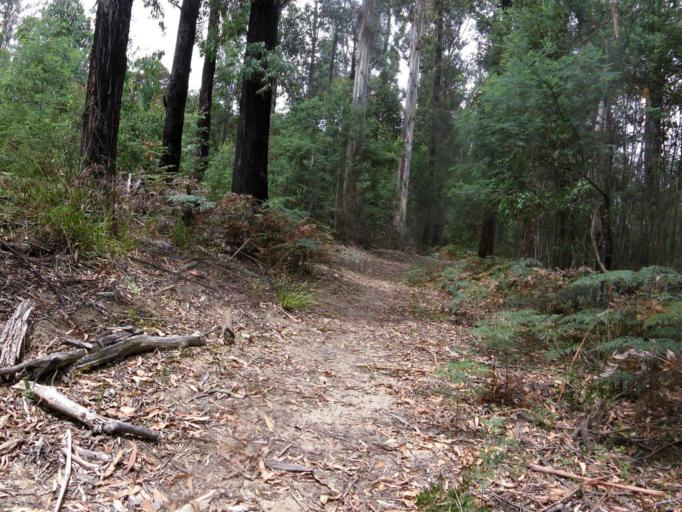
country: AU
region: Victoria
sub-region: Yarra Ranges
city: Healesville
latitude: -37.4435
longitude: 145.5829
